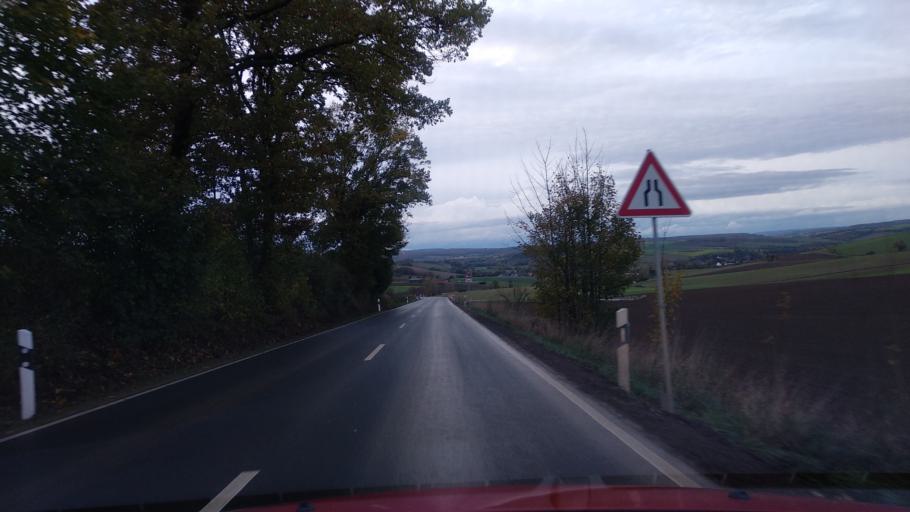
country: DE
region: North Rhine-Westphalia
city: Brakel
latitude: 51.6694
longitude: 9.2354
